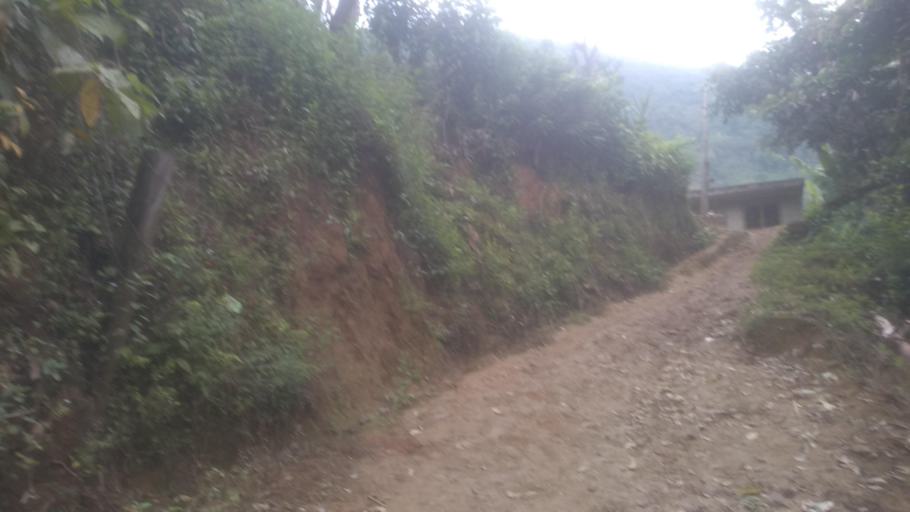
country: MX
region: Veracruz
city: Chocaman
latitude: 18.9958
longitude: -97.0592
